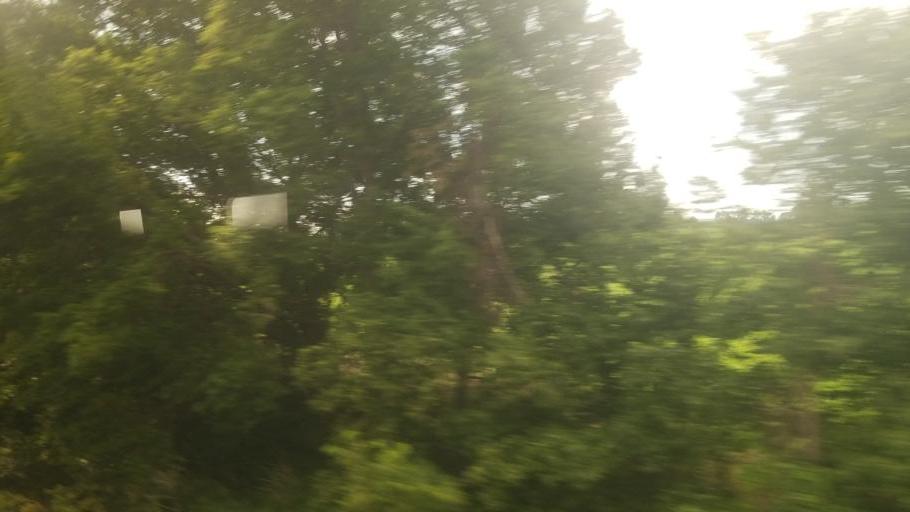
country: US
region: Kansas
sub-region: Douglas County
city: Eudora
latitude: 38.9499
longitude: -95.1636
